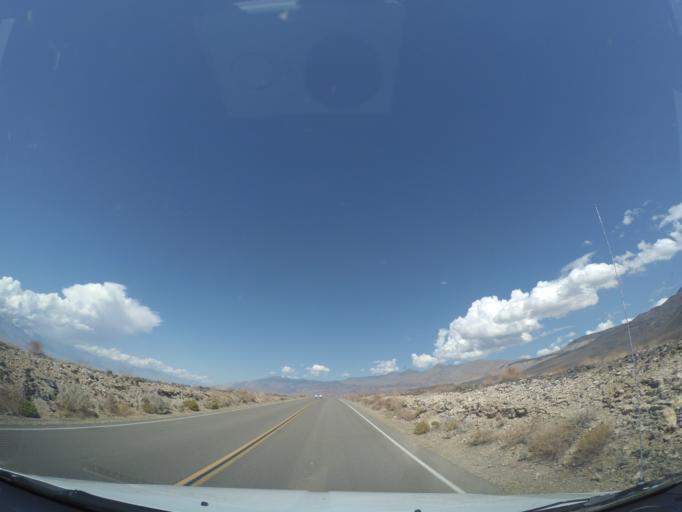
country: US
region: California
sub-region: Inyo County
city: Lone Pine
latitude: 36.4076
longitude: -117.8108
